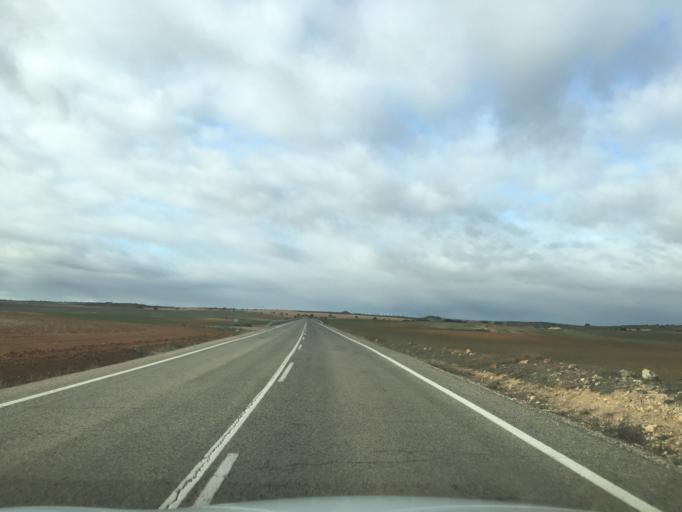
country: ES
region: Castille-La Mancha
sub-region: Provincia de Albacete
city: Petrola
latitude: 38.8265
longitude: -1.5741
